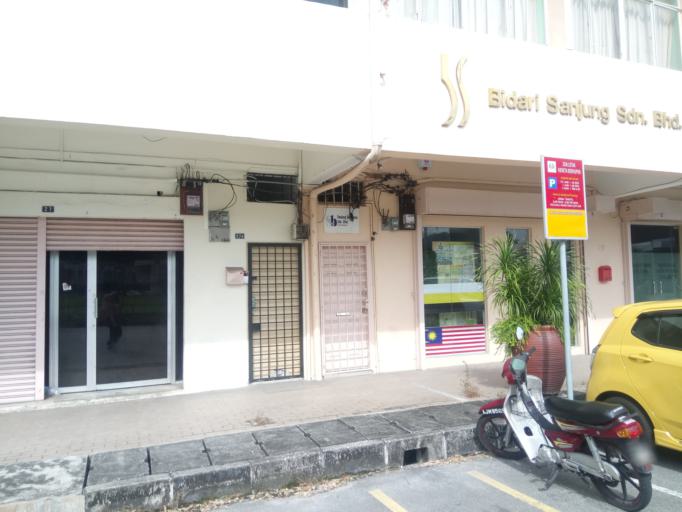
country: MY
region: Perak
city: Ipoh
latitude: 4.6058
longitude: 101.0817
